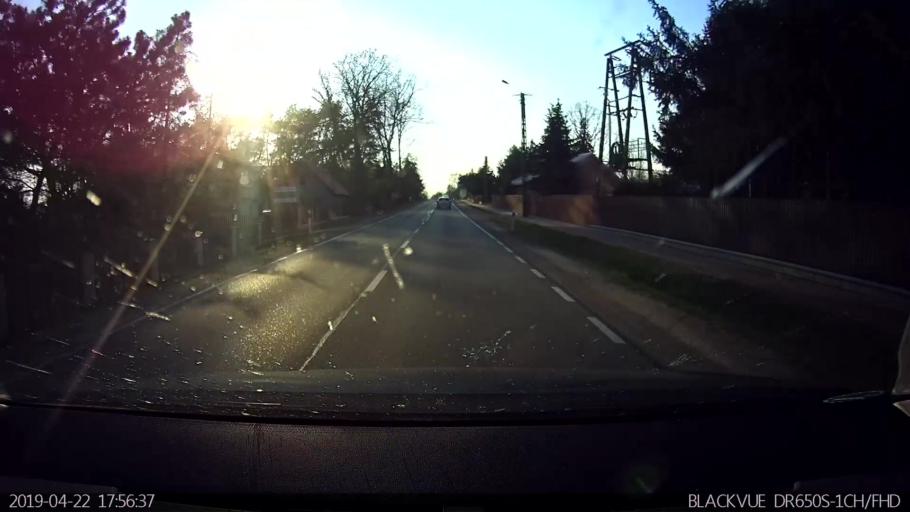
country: PL
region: Masovian Voivodeship
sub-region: Powiat wegrowski
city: Korytnica
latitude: 52.4657
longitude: 21.9046
